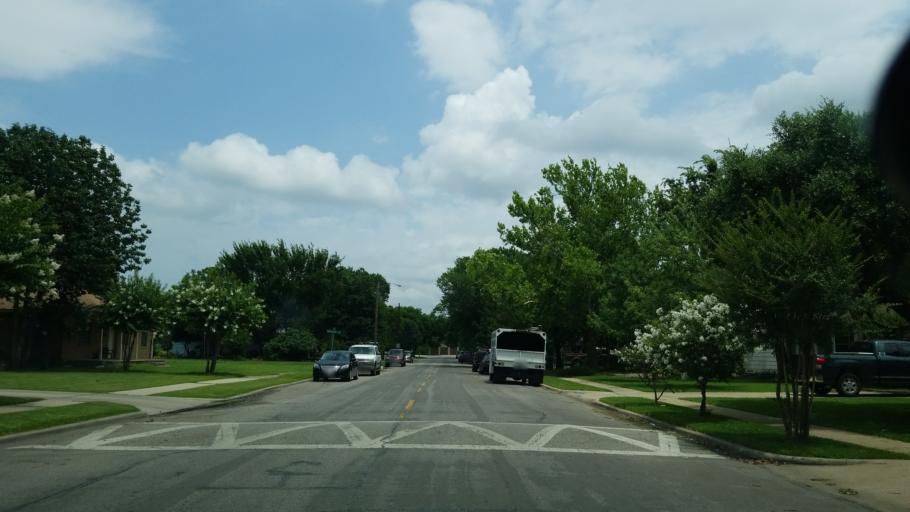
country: US
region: Texas
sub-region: Dallas County
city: University Park
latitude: 32.8750
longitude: -96.8584
